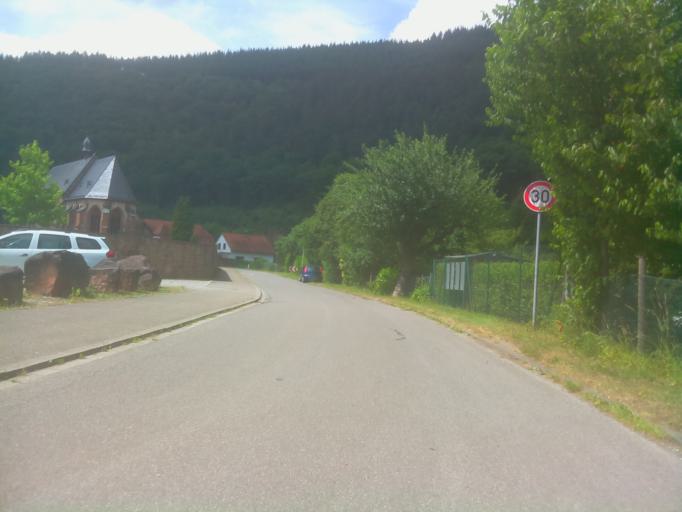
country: DE
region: Hesse
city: Hirschhorn
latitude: 49.4522
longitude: 8.9109
